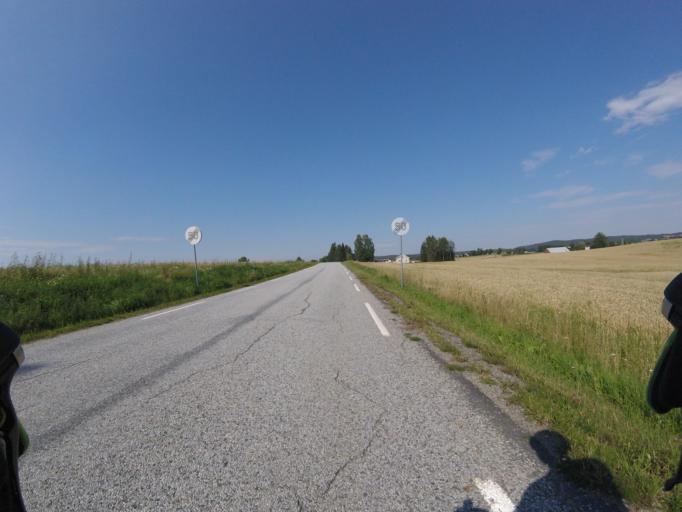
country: NO
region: Akershus
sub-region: Ullensaker
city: Klofta
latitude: 60.0880
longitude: 11.1621
